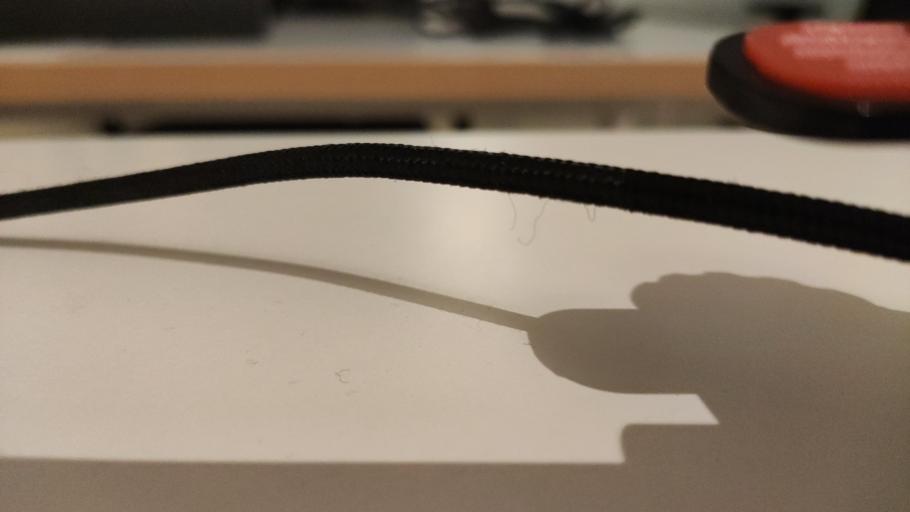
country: RU
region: Moskovskaya
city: Shaburnovo
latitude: 56.4335
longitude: 37.9307
